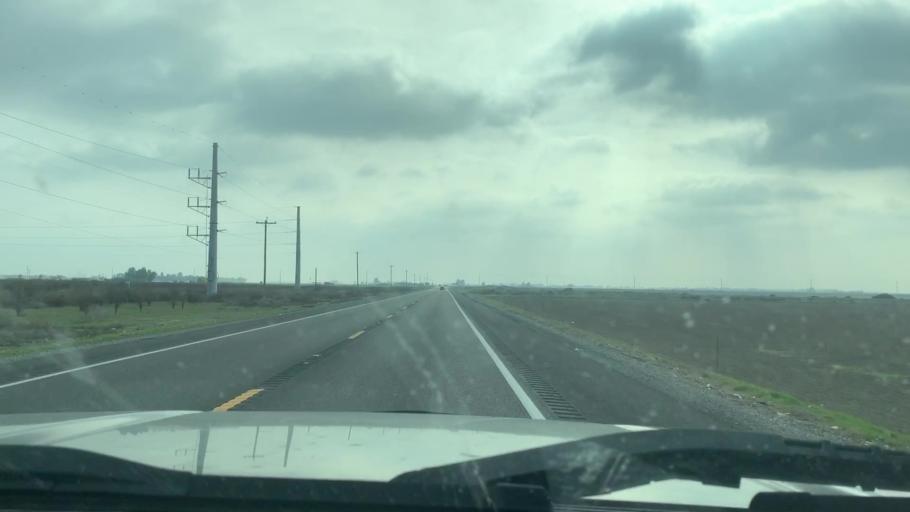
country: US
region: California
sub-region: Kings County
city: Stratford
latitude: 36.2349
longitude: -119.8164
